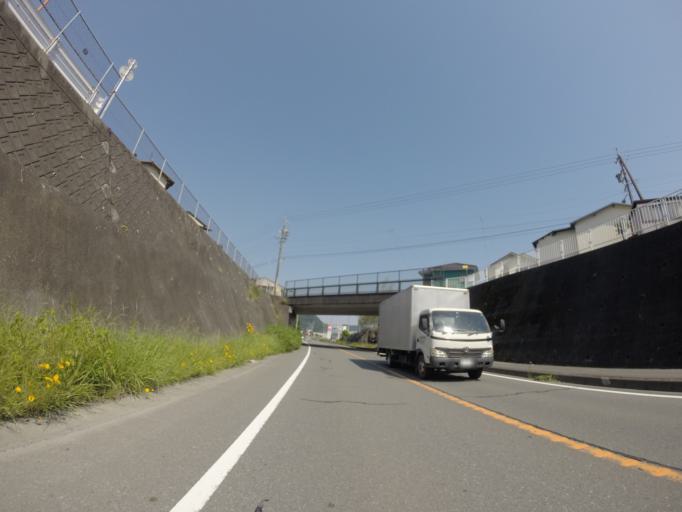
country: JP
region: Shizuoka
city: Fujinomiya
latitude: 35.1883
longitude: 138.5939
